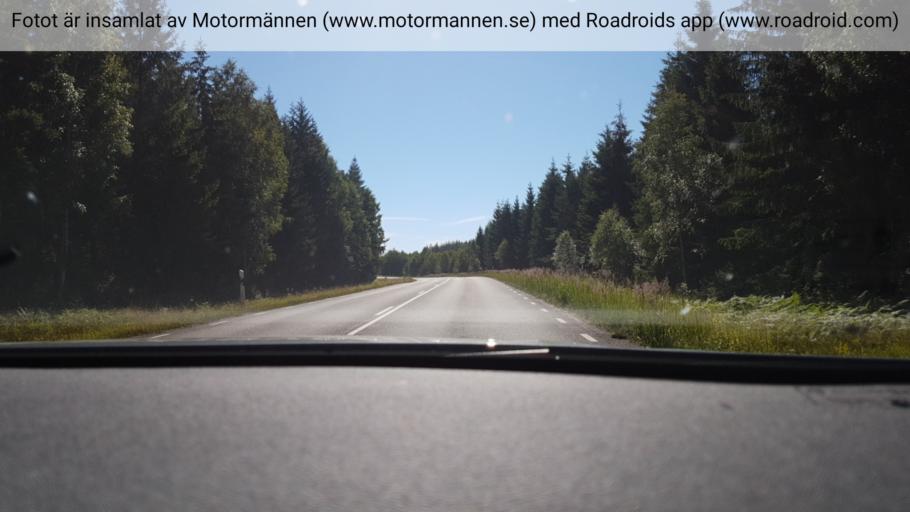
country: SE
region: Vaestra Goetaland
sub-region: Tidaholms Kommun
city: Tidaholm
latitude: 58.1925
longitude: 13.8989
